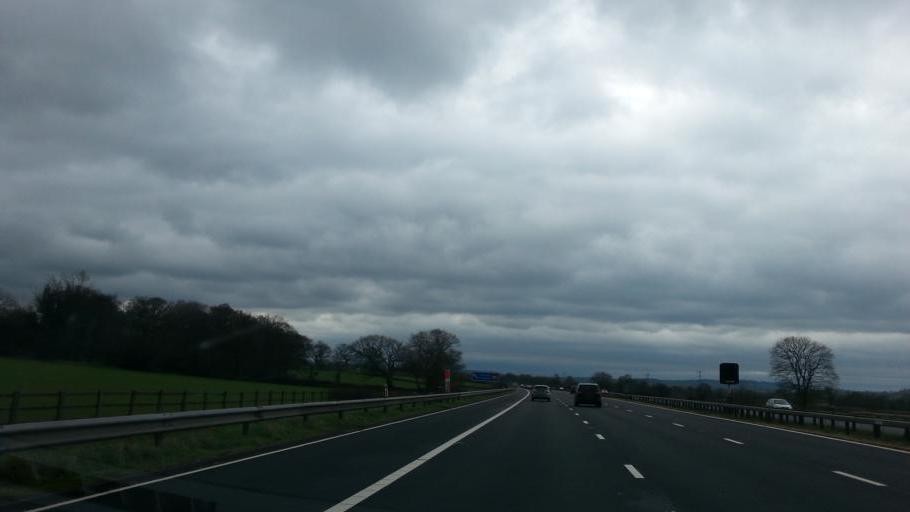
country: GB
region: England
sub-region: Devon
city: Uffculme
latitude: 50.9256
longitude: -3.3444
